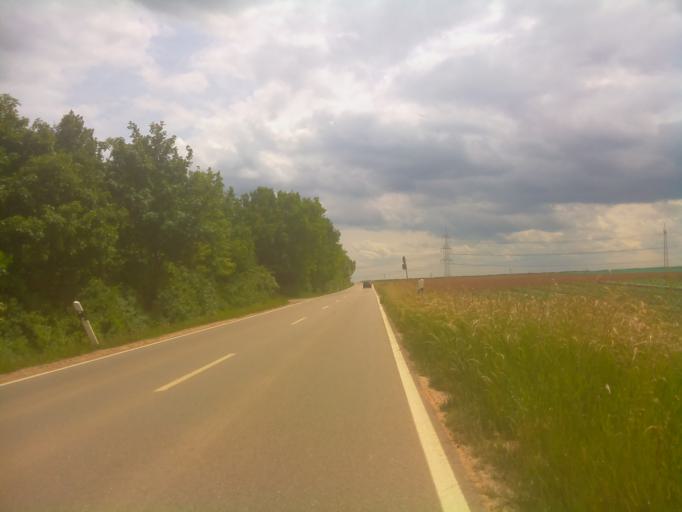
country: DE
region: Rheinland-Pfalz
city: Gerolsheim
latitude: 49.5344
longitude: 8.2796
